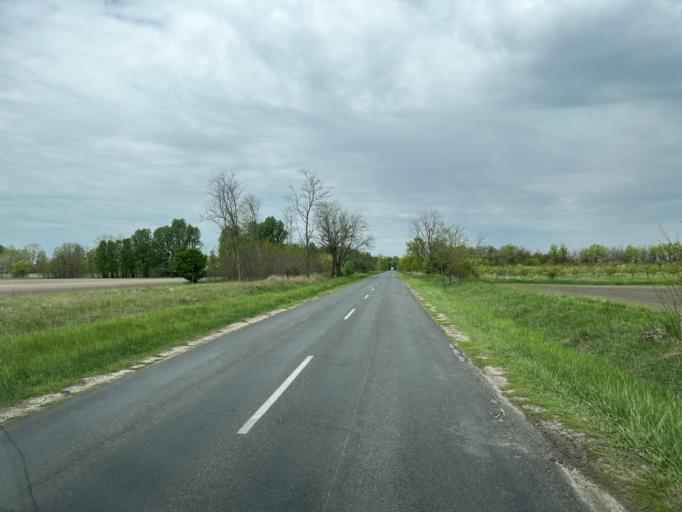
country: HU
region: Pest
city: Cegled
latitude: 47.1586
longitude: 19.8488
